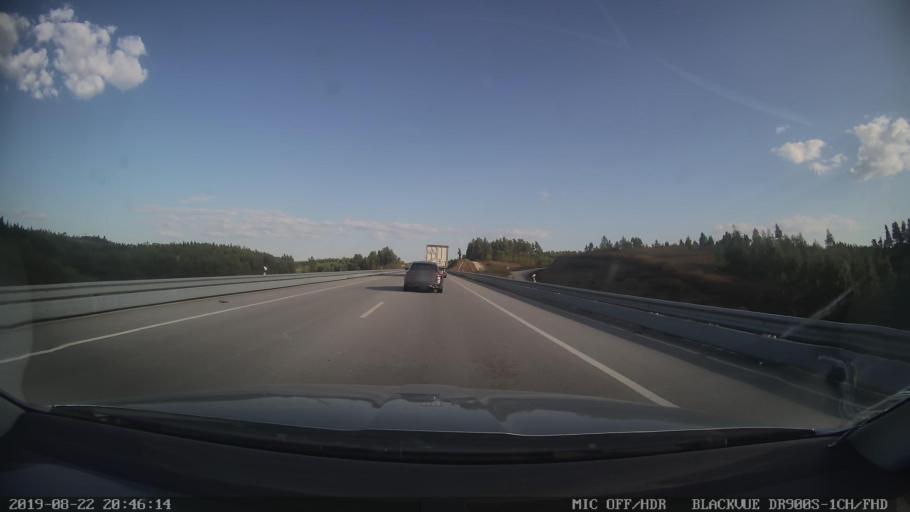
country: PT
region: Castelo Branco
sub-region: Proenca-A-Nova
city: Proenca-a-Nova
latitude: 39.7247
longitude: -7.8745
